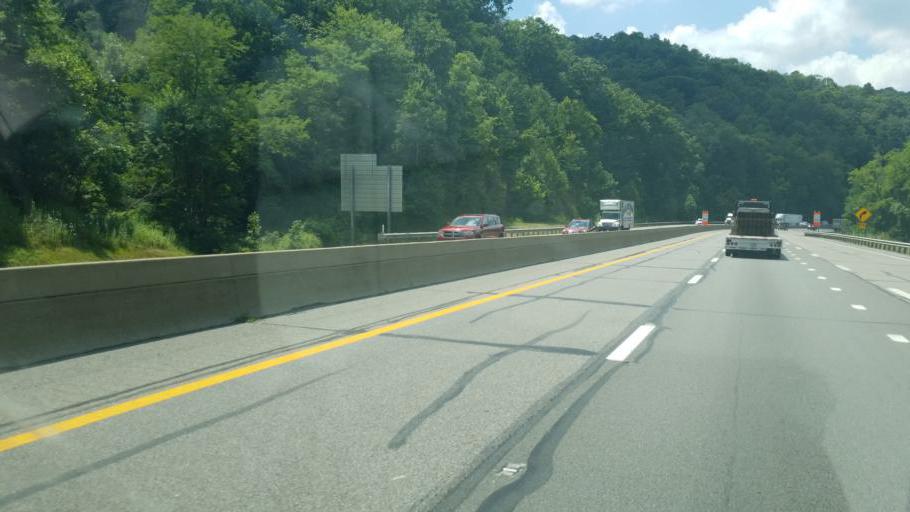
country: US
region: West Virginia
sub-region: Fayette County
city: Oak Hill
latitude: 37.9738
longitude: -81.2896
